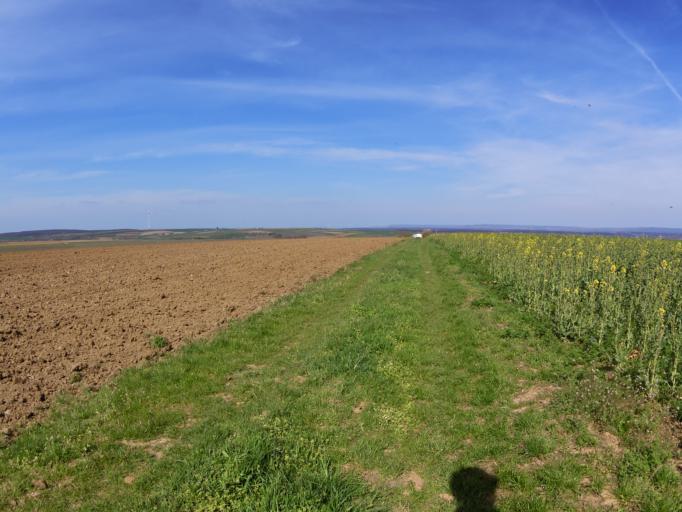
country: DE
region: Bavaria
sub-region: Regierungsbezirk Unterfranken
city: Mainstockheim
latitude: 49.7981
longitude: 10.1396
